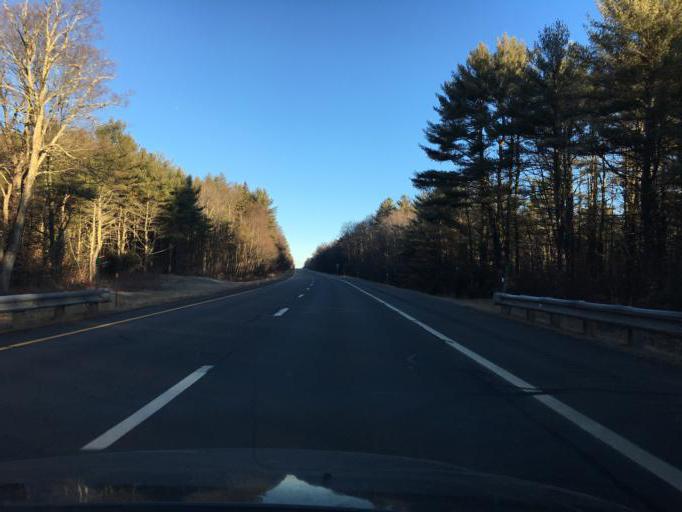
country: US
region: New Hampshire
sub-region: Belknap County
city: Sanbornton
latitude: 43.5263
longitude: -71.6121
